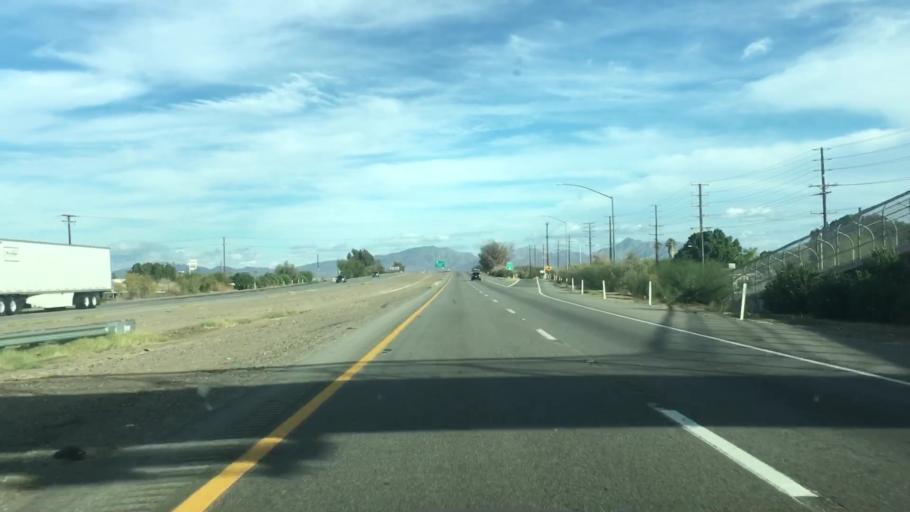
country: US
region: California
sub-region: Riverside County
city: Blythe
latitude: 33.6070
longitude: -114.5931
